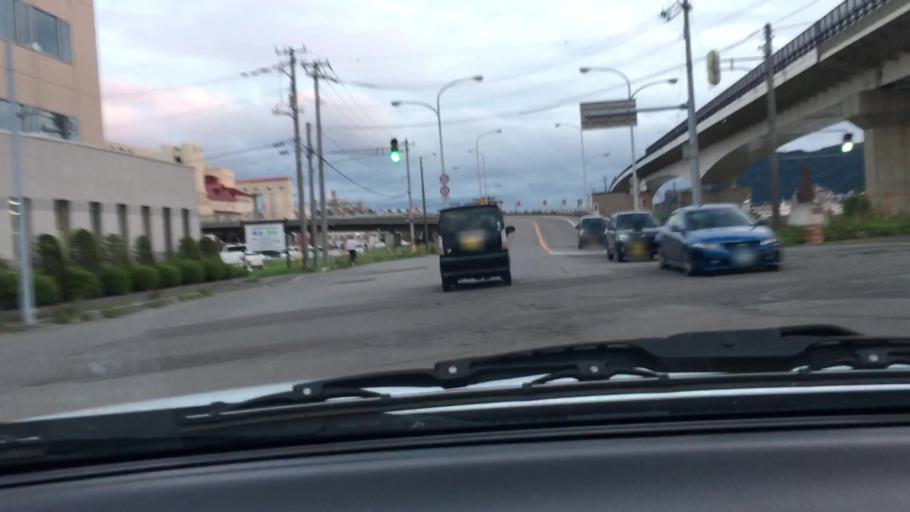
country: JP
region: Hokkaido
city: Hakodate
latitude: 41.7829
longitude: 140.7270
